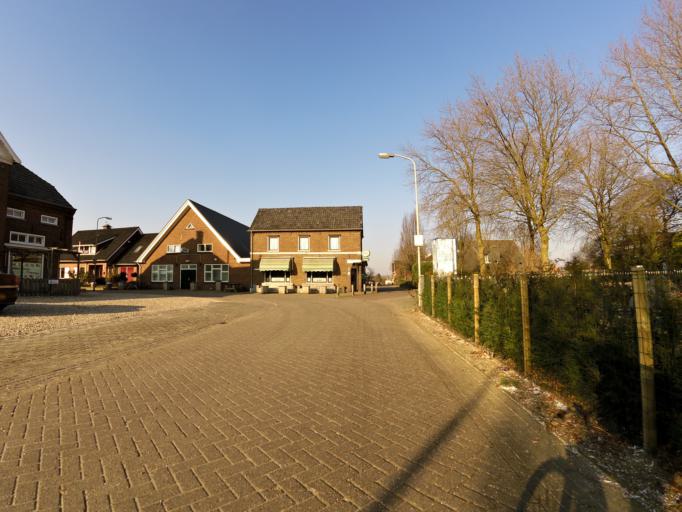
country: NL
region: Gelderland
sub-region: Gemeente Montferland
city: s-Heerenberg
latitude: 51.8863
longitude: 6.3046
